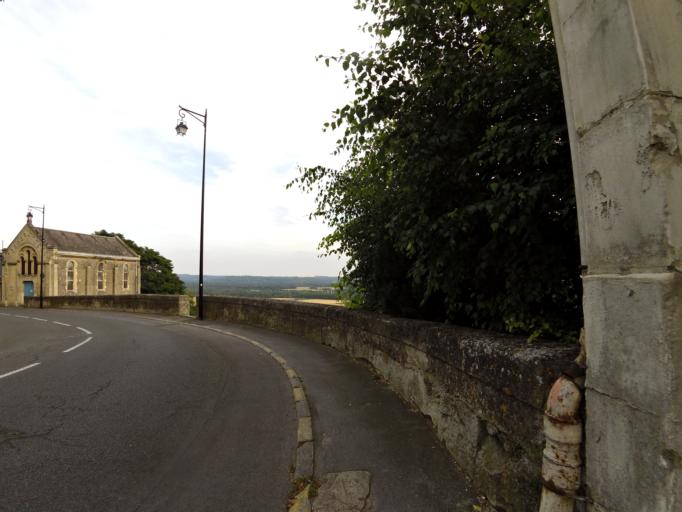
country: FR
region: Picardie
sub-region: Departement de l'Aisne
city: Laon
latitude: 49.5617
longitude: 3.6219
